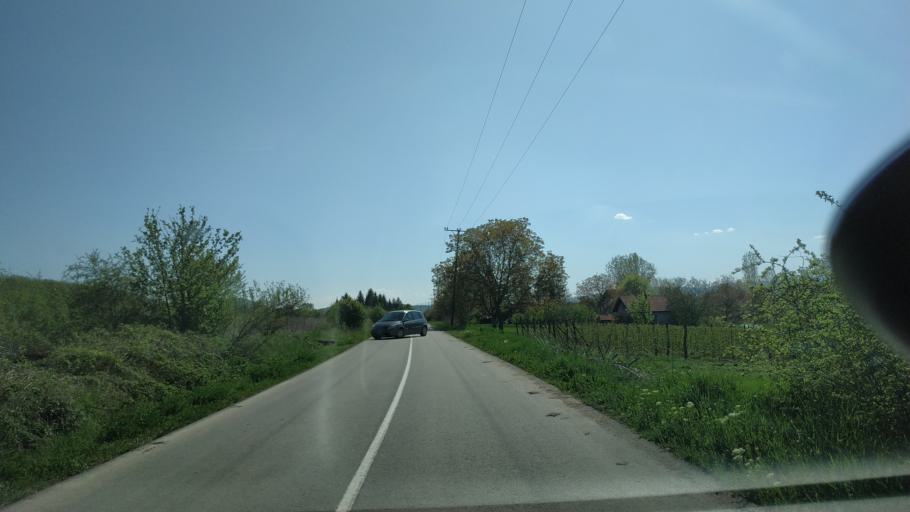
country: RS
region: Central Serbia
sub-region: Nisavski Okrug
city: Nis
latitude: 43.4583
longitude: 21.8548
